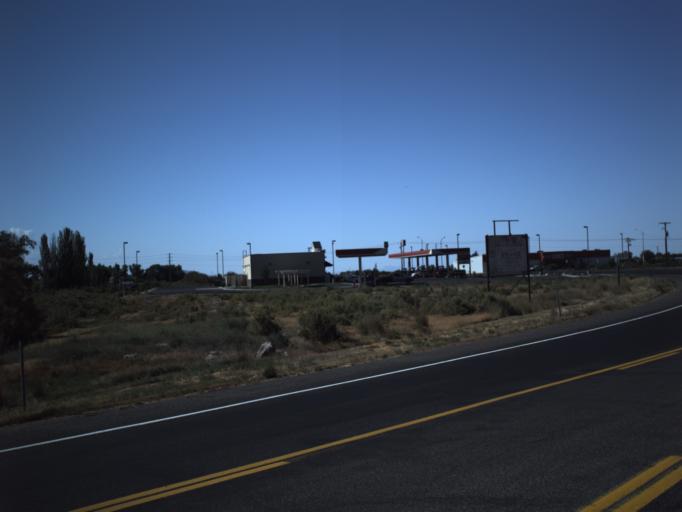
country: US
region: Utah
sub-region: Millard County
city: Delta
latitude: 39.3548
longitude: -112.5627
